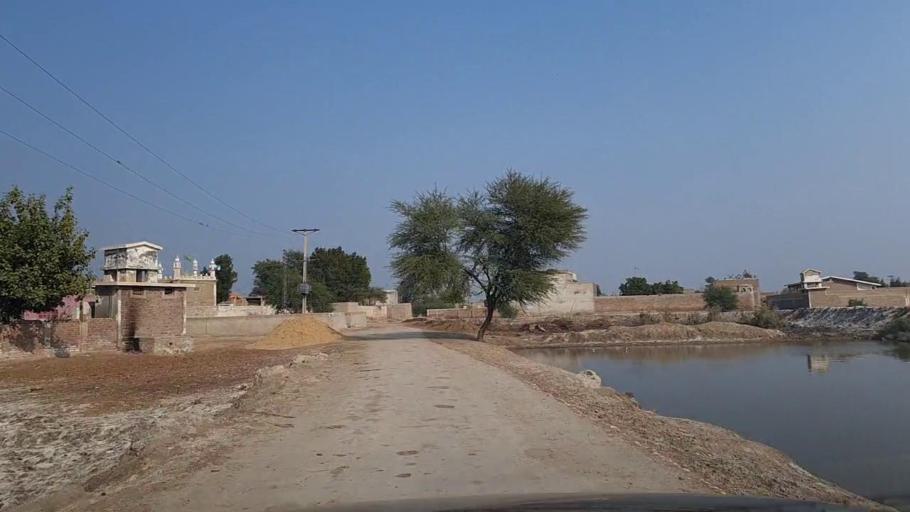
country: PK
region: Sindh
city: Daur
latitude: 26.4137
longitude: 68.4113
